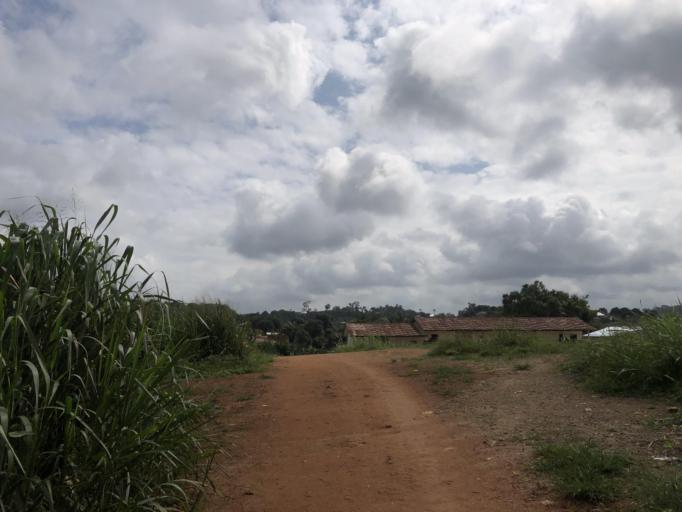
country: SL
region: Eastern Province
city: Kailahun
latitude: 8.2780
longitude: -10.5662
